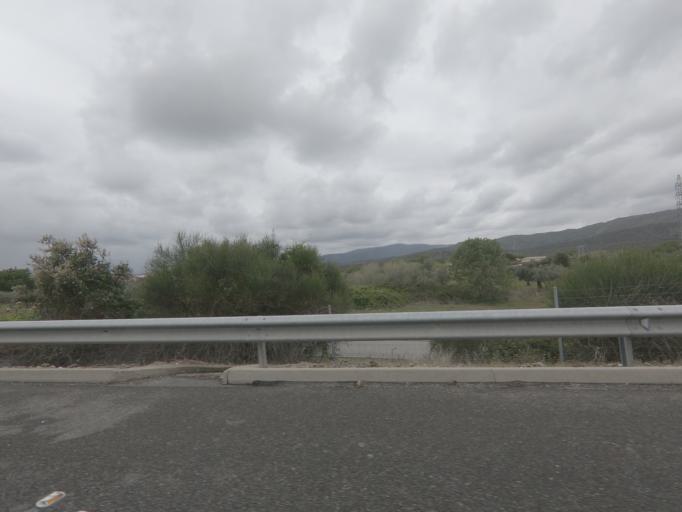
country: ES
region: Extremadura
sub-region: Provincia de Caceres
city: Aldeanueva del Camino
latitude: 40.2597
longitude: -5.9181
